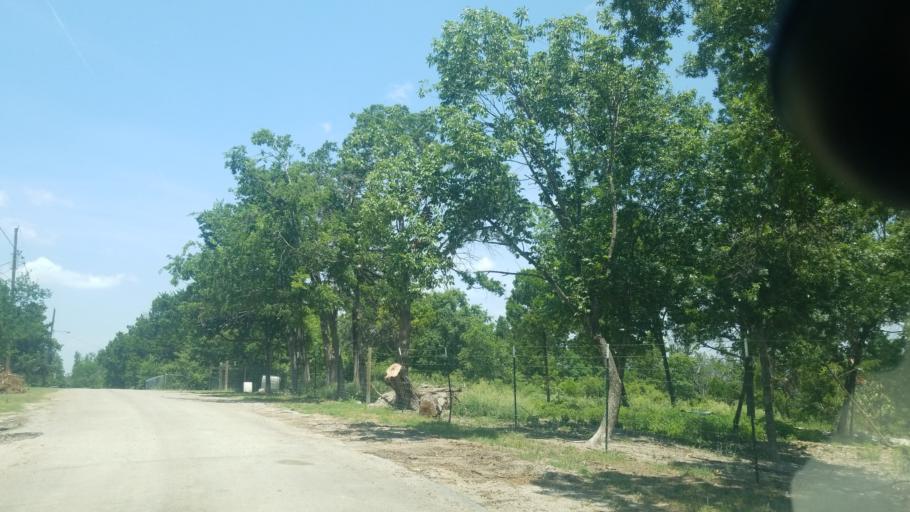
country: US
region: Texas
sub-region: Dallas County
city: Dallas
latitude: 32.7326
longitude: -96.7876
